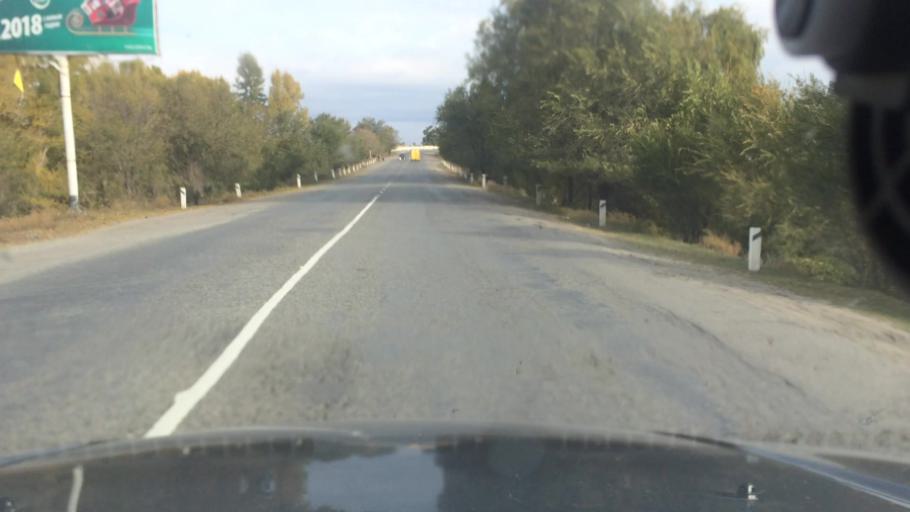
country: KG
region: Ysyk-Koel
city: Karakol
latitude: 42.5335
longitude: 78.3818
